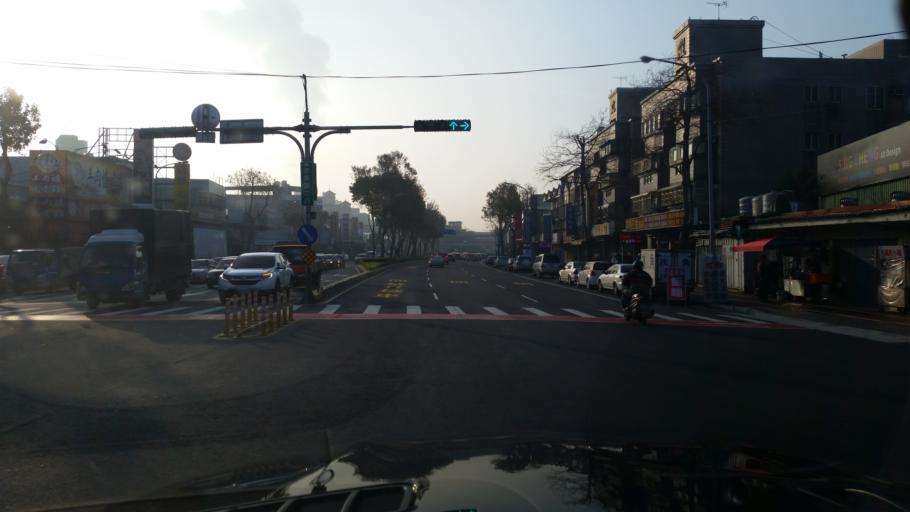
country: TW
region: Taiwan
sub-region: Taoyuan
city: Taoyuan
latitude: 25.0559
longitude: 121.3576
